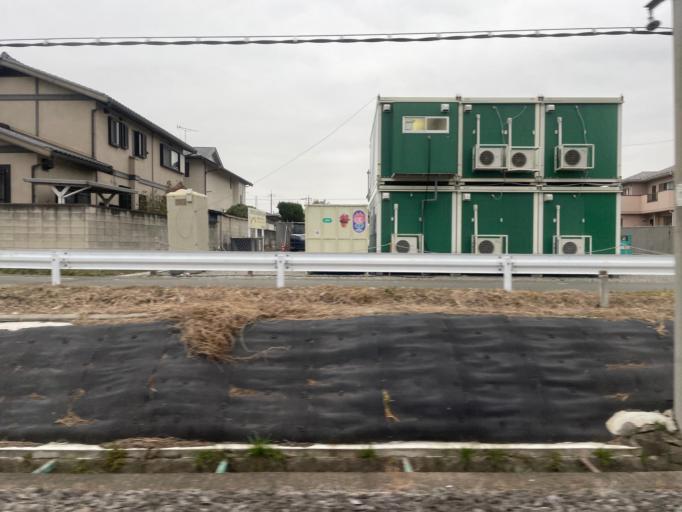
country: JP
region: Gunma
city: Kanekomachi
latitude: 36.4271
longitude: 139.0298
